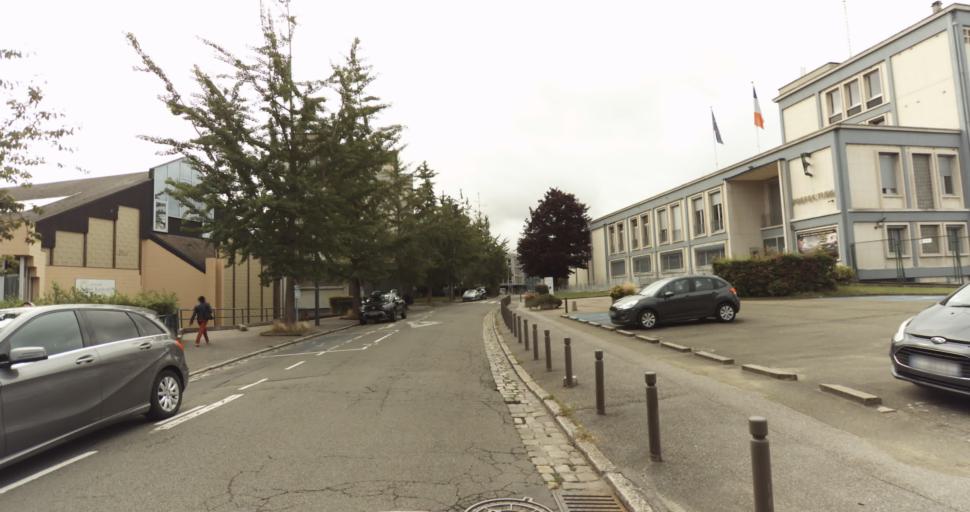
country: FR
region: Haute-Normandie
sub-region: Departement de l'Eure
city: Evreux
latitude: 49.0260
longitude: 1.1427
